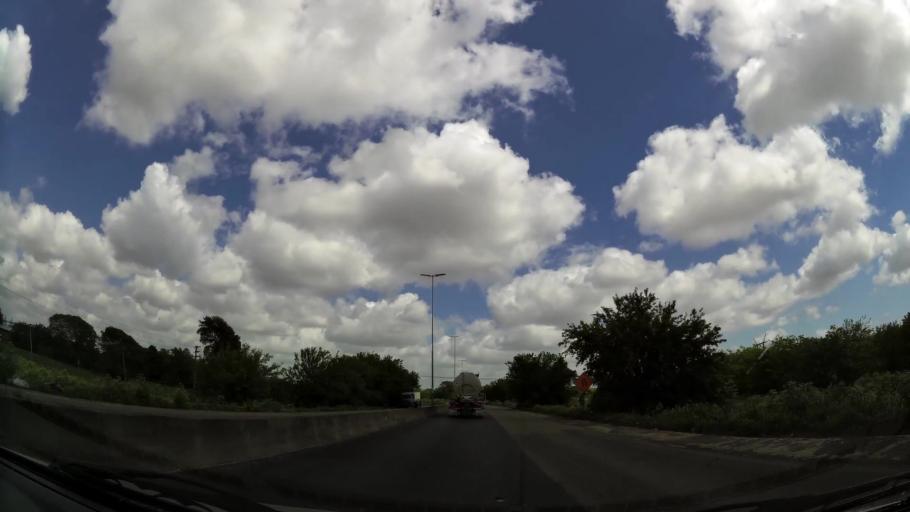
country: AR
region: Buenos Aires
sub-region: Partido de Quilmes
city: Quilmes
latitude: -34.8332
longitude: -58.2076
